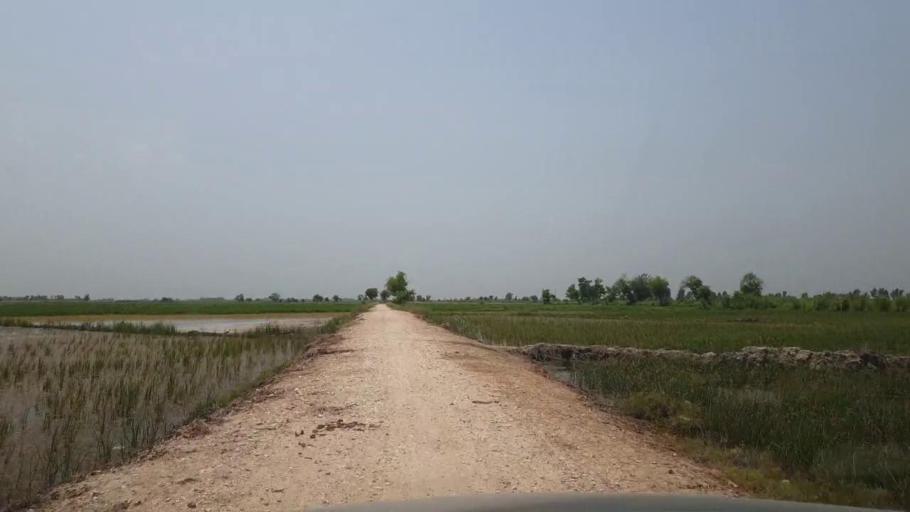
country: PK
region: Sindh
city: Garhi Yasin
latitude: 27.8675
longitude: 68.4869
